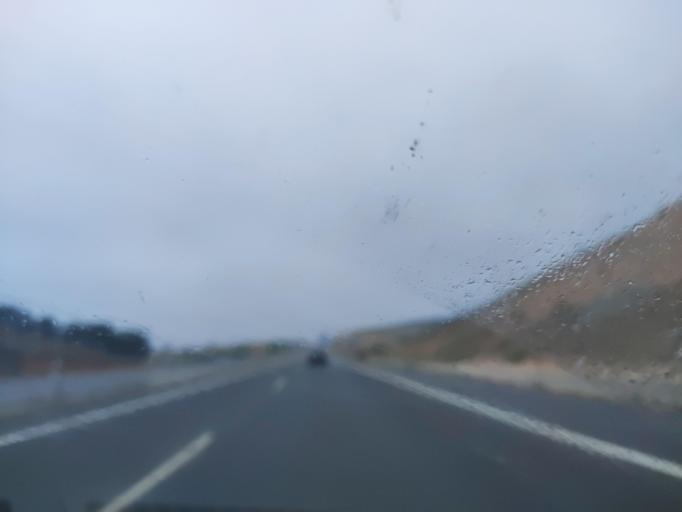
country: ES
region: Castille-La Mancha
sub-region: Province of Toledo
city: Bargas
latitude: 39.9132
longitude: -4.0496
